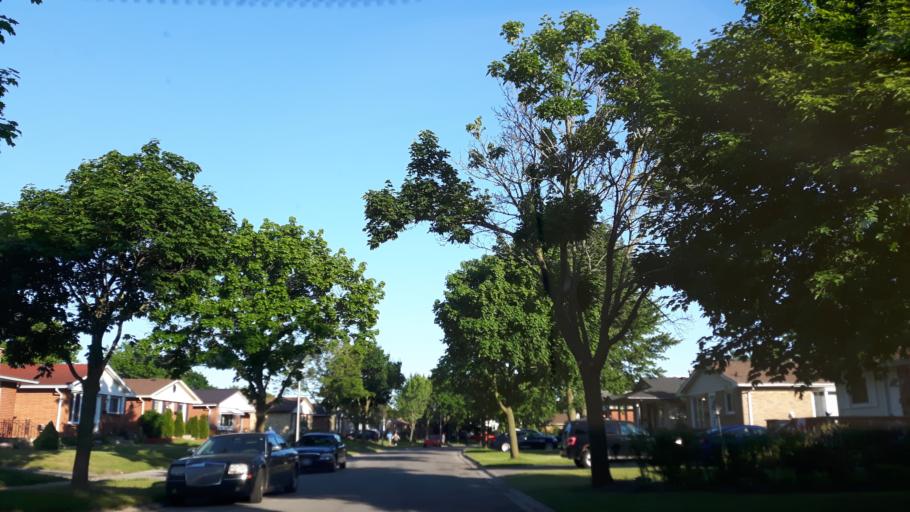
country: CA
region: Ontario
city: London
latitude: 42.9397
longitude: -81.2083
